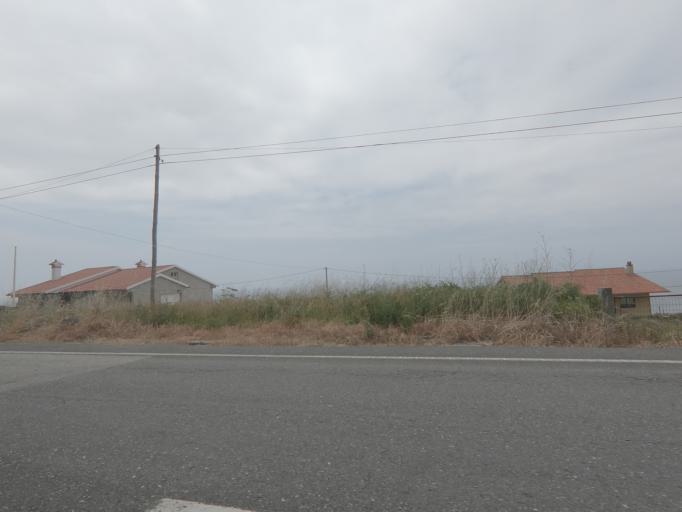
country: ES
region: Galicia
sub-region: Provincia de Pontevedra
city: Oia
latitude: 41.9979
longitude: -8.8763
